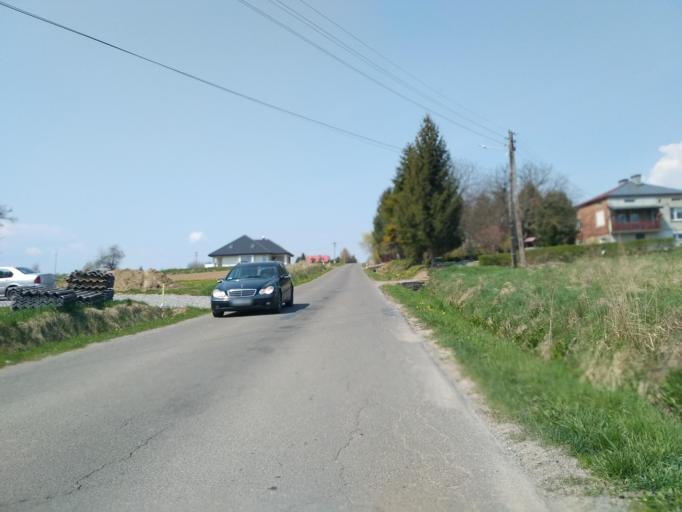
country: PL
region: Subcarpathian Voivodeship
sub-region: Powiat krosnienski
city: Chorkowka
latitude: 49.6609
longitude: 21.6474
